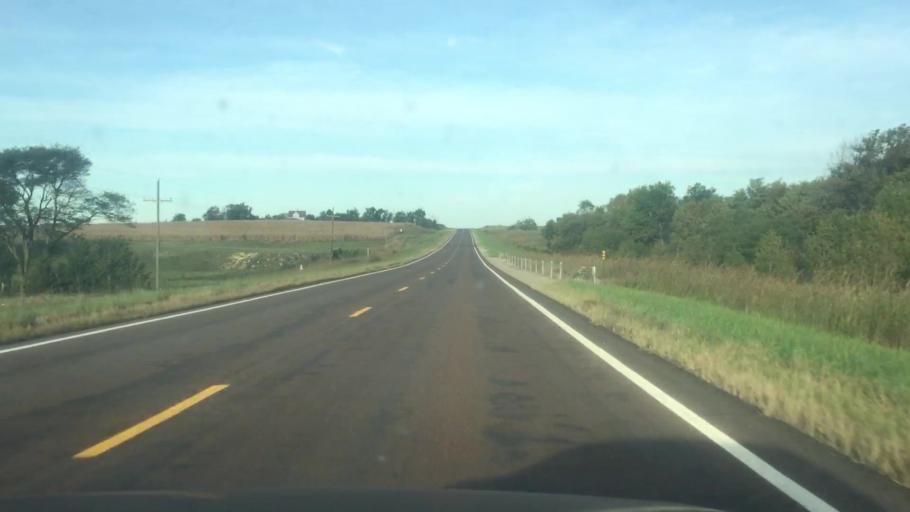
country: US
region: Nebraska
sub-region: Gage County
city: Wymore
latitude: 40.0458
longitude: -96.8352
